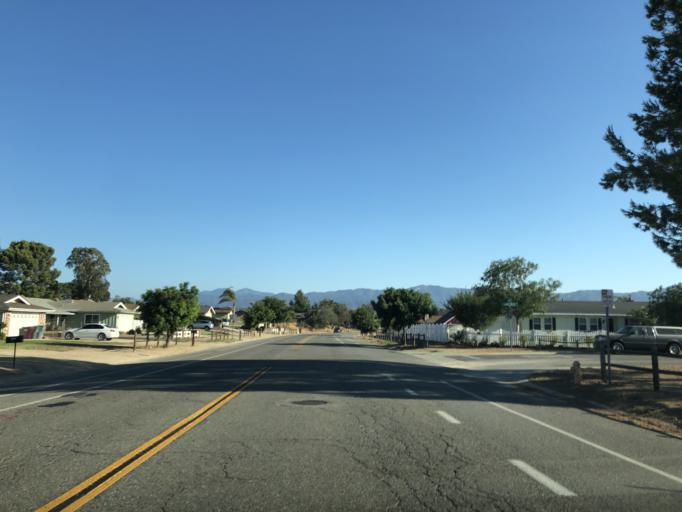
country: US
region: California
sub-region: Riverside County
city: Norco
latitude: 33.9216
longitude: -117.5823
